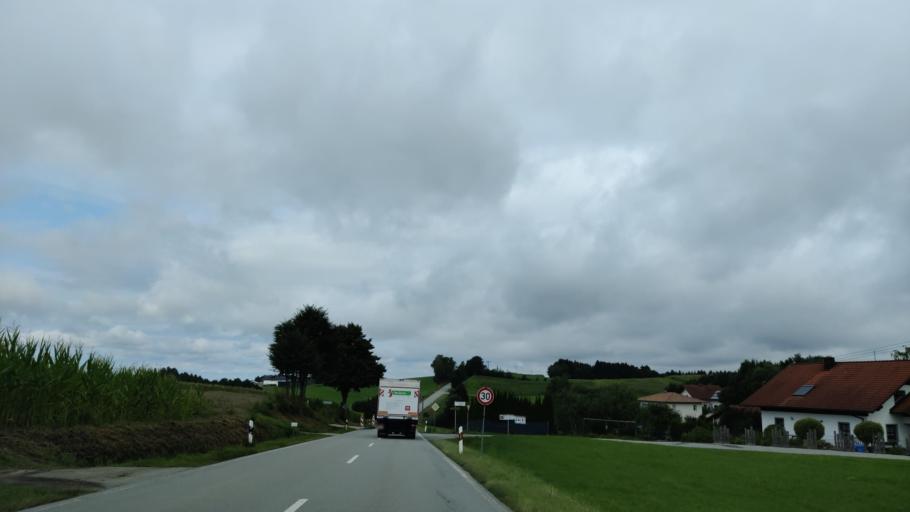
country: DE
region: Bavaria
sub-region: Lower Bavaria
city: Hofkirchen
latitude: 48.6751
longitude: 13.1622
